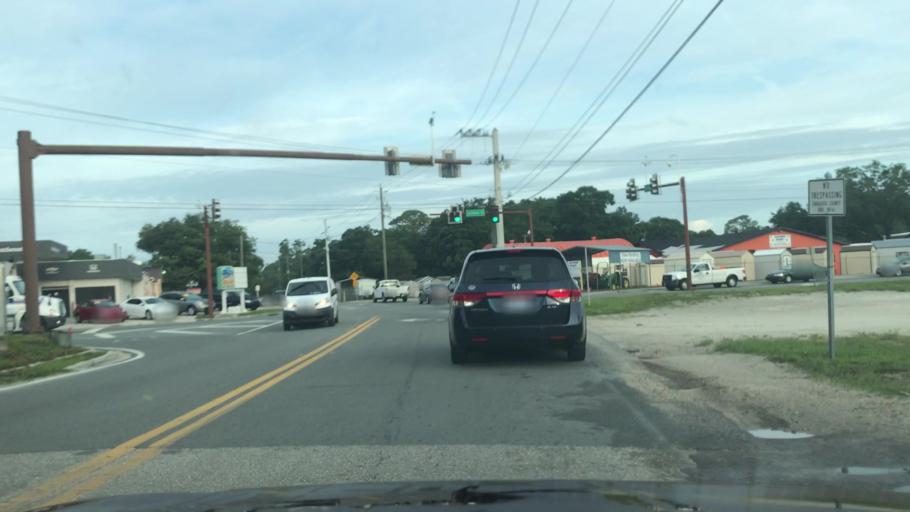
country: US
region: Florida
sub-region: Sarasota County
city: Fruitville
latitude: 27.3268
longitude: -82.4509
